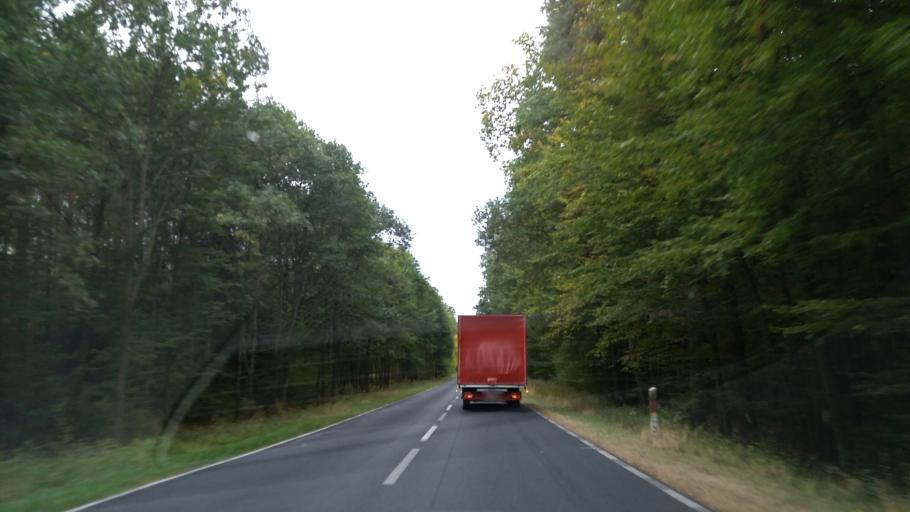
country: PL
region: West Pomeranian Voivodeship
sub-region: Powiat mysliborski
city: Barlinek
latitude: 52.9287
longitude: 15.1939
